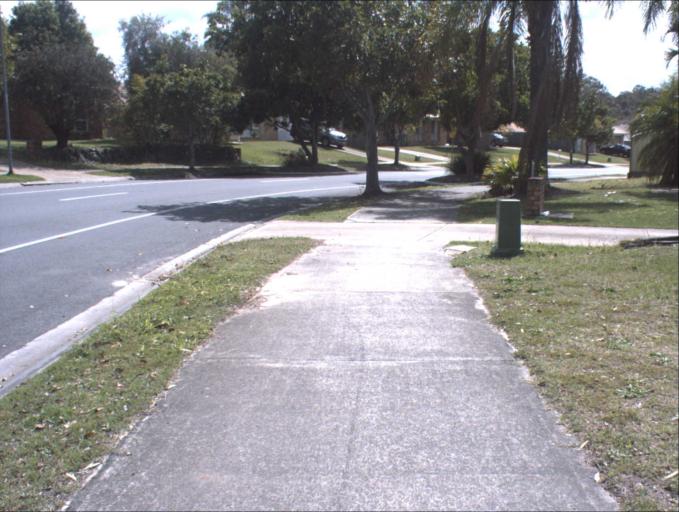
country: AU
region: Queensland
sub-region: Logan
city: Park Ridge South
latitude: -27.6947
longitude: 153.0195
